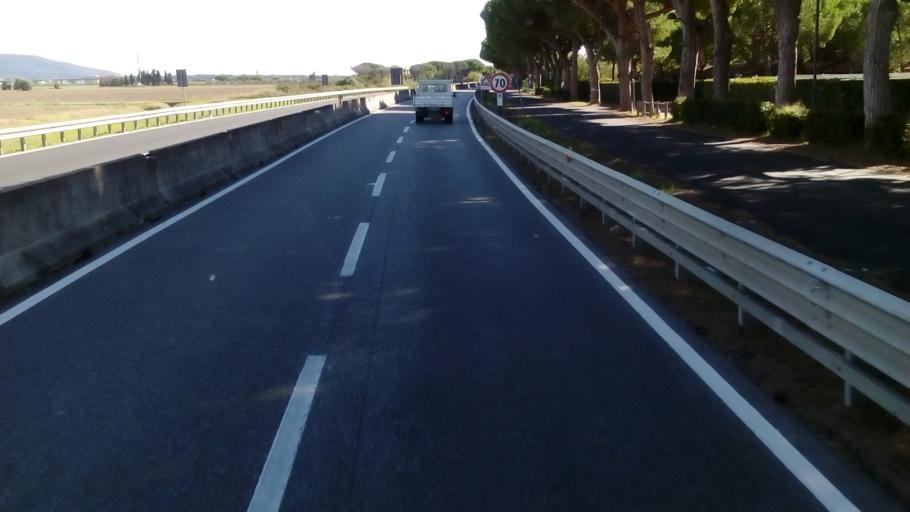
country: IT
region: Tuscany
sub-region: Provincia di Grosseto
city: Albinia
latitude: 42.5203
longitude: 11.1925
